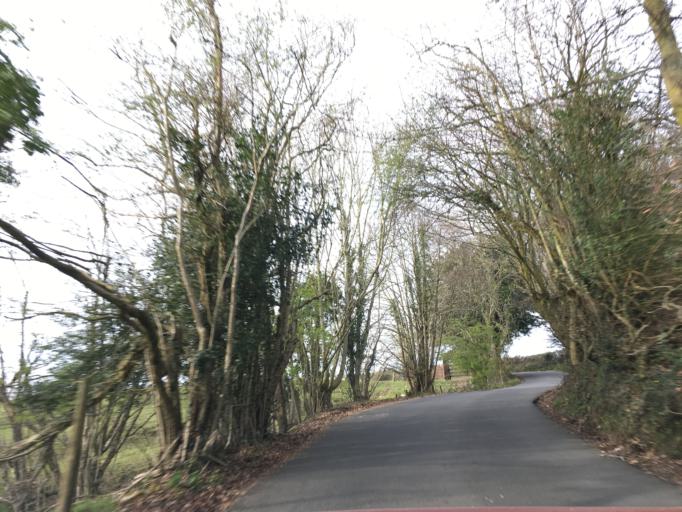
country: GB
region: Wales
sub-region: Caerphilly County Borough
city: Maesycwmmer
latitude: 51.6255
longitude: -3.2191
